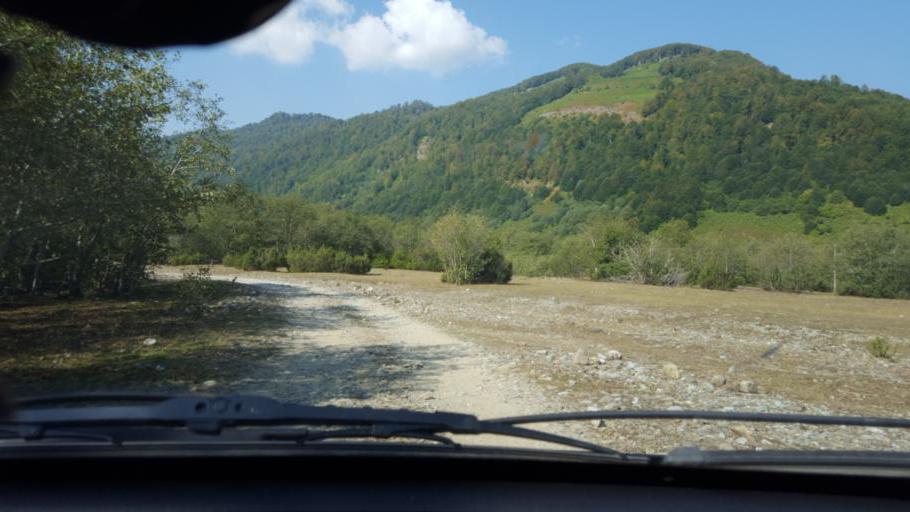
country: ME
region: Andrijevica
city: Andrijevica
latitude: 42.5976
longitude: 19.6578
